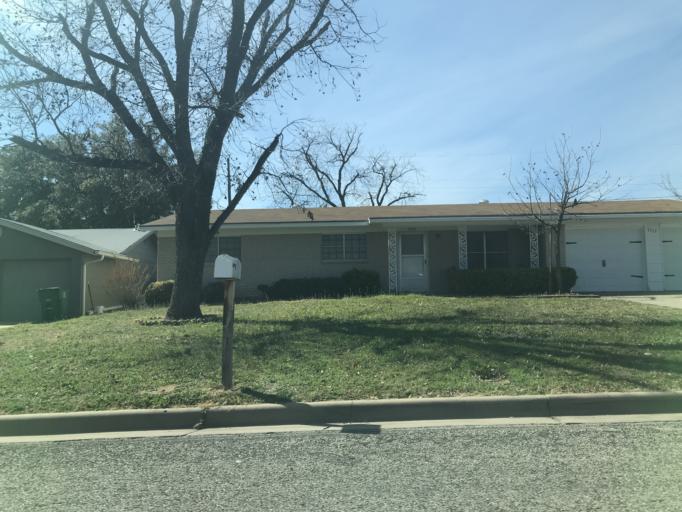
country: US
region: Texas
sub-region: Tom Green County
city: San Angelo
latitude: 31.4411
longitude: -100.4788
